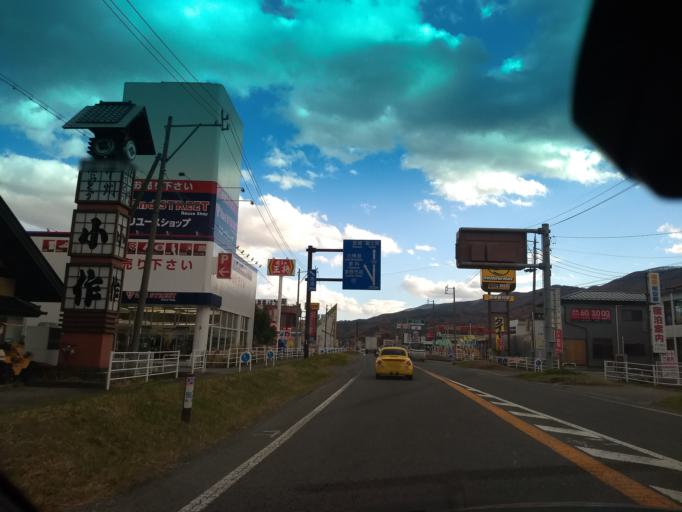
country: JP
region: Nagano
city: Chino
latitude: 36.0032
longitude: 138.1331
